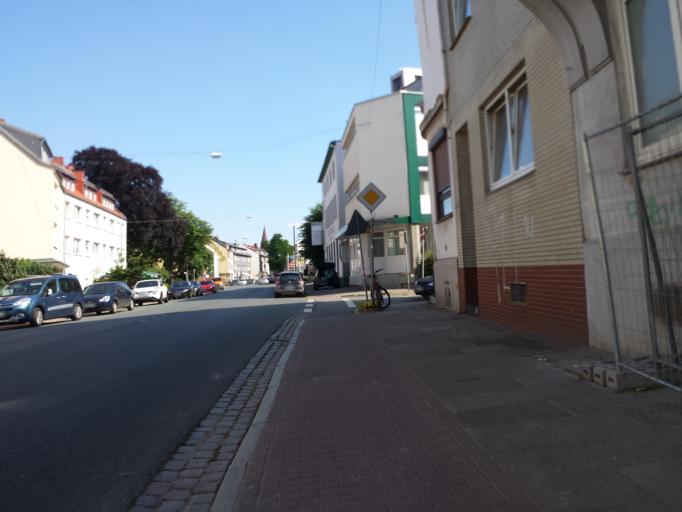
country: DE
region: Bremen
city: Bremen
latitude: 53.0865
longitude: 8.7633
